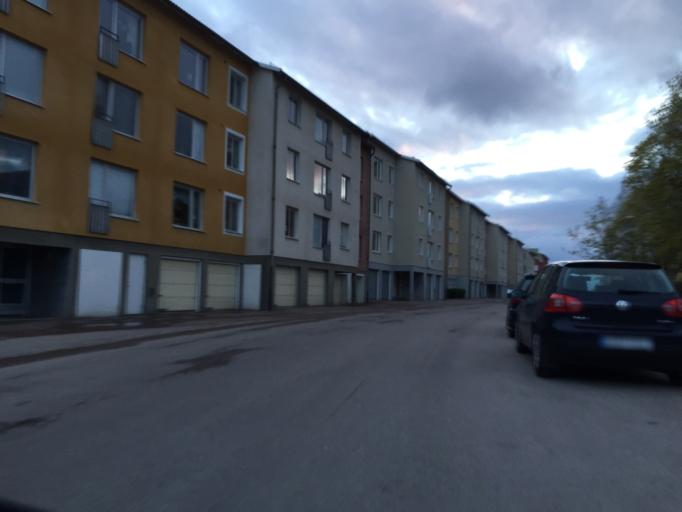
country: SE
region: Dalarna
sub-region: Ludvika Kommun
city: Ludvika
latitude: 60.1472
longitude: 15.1916
